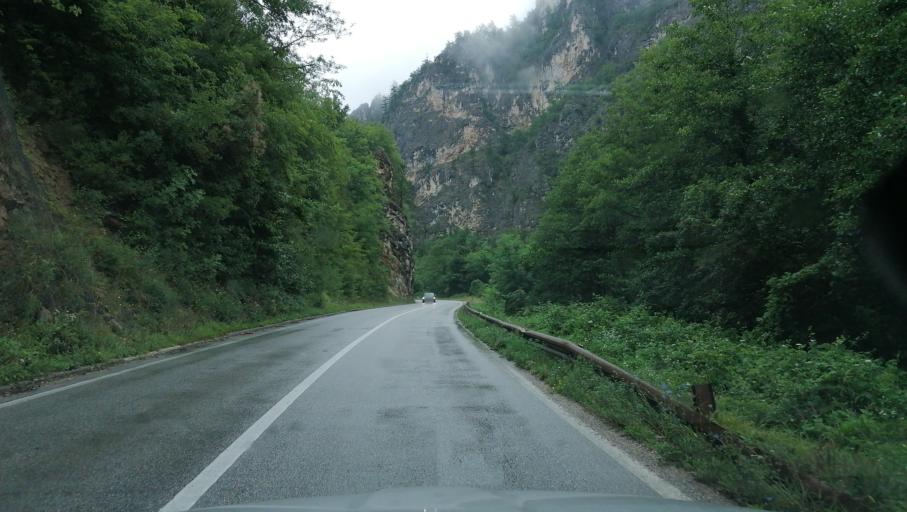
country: RS
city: Durici
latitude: 43.7513
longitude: 19.4001
